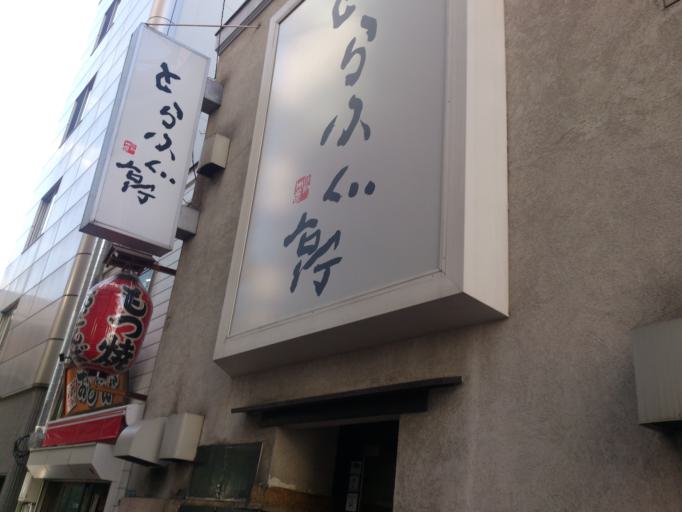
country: JP
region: Tokyo
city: Tokyo
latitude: 35.7101
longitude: 139.7760
